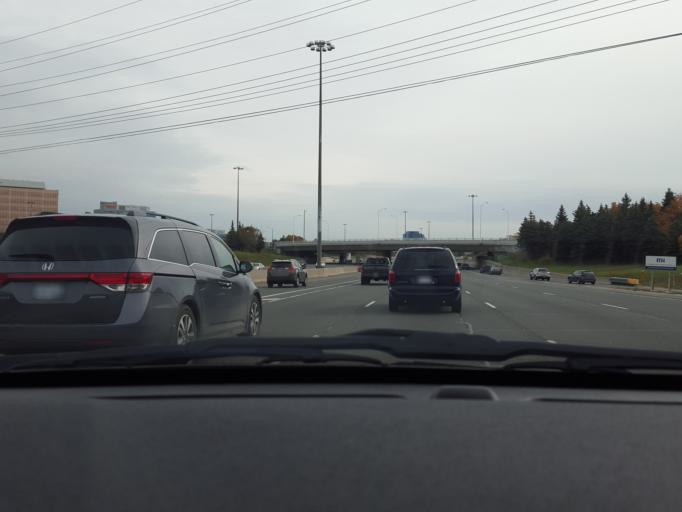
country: CA
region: Ontario
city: Willowdale
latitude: 43.8141
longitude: -79.3550
